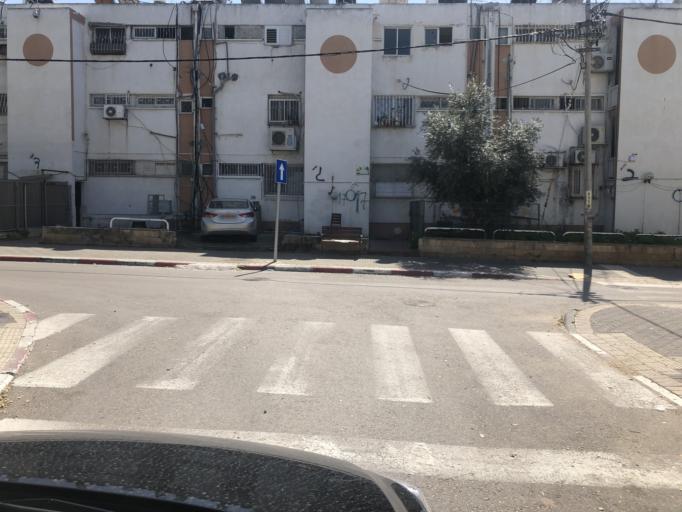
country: IL
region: Tel Aviv
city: Holon
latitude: 32.0020
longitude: 34.7624
